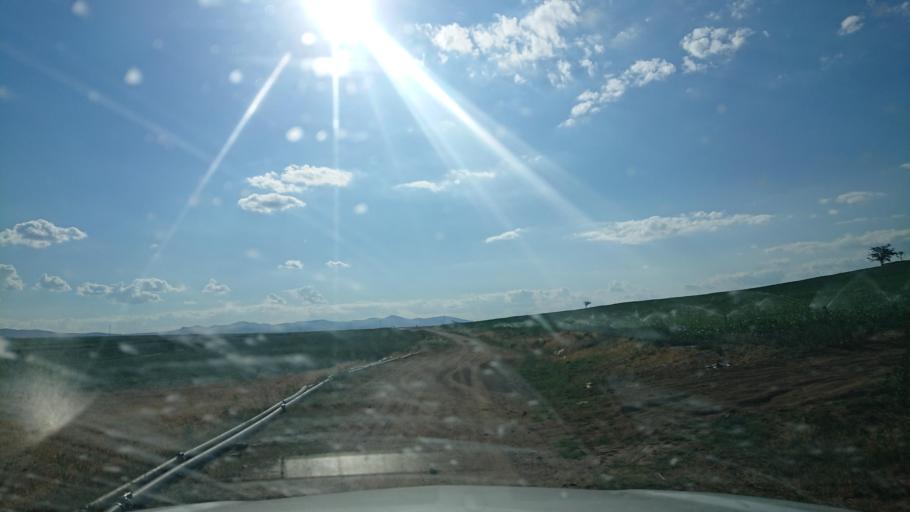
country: TR
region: Aksaray
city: Sariyahsi
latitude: 39.0194
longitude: 33.8914
